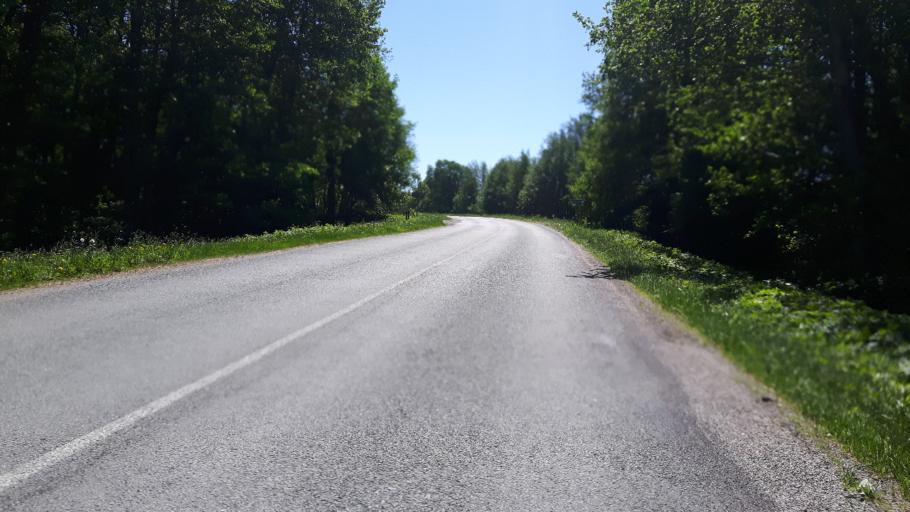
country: EE
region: Harju
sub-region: Kuusalu vald
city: Kuusalu
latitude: 59.5119
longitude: 25.5189
